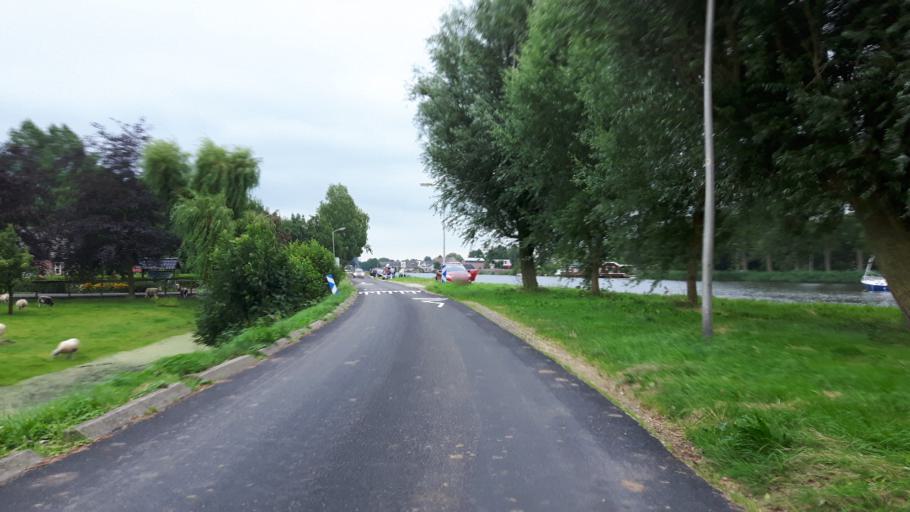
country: NL
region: South Holland
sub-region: Bodegraven-Reeuwijk
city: Bodegraven
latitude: 52.1102
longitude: 4.7161
